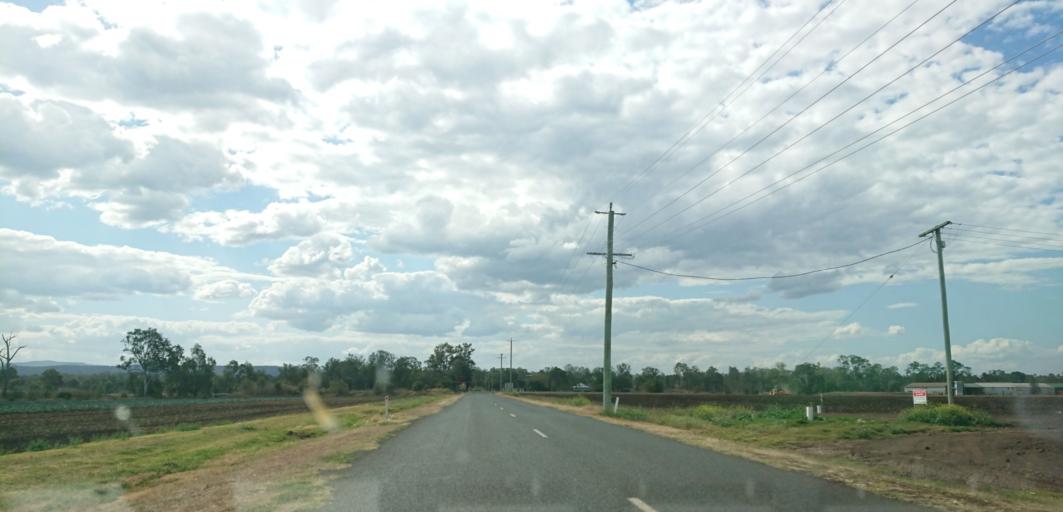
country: AU
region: Queensland
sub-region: Lockyer Valley
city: Gatton
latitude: -27.5781
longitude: 152.2296
